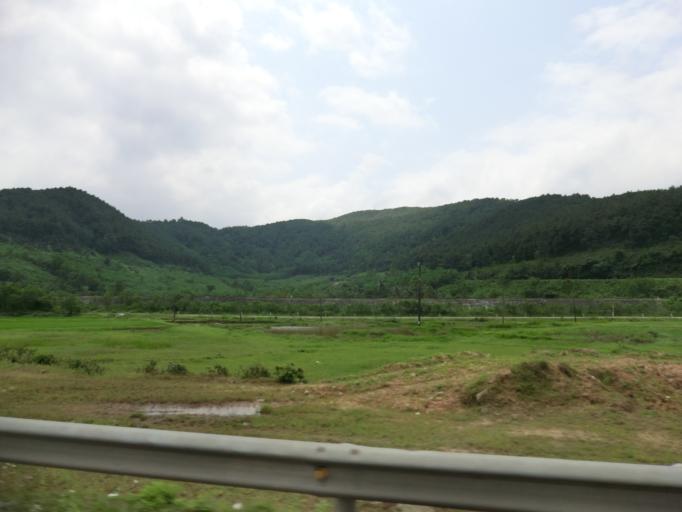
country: VN
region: Thua Thien-Hue
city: Phu Loc
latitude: 16.2819
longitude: 107.9097
